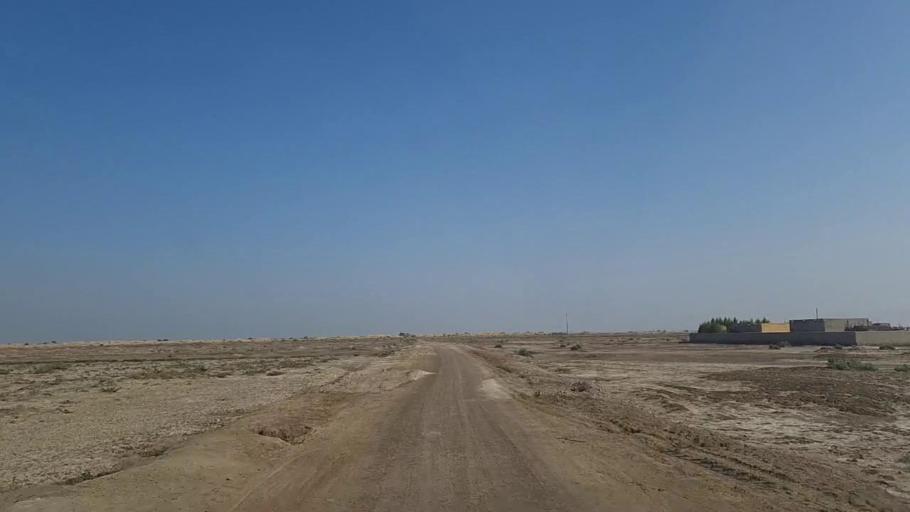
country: PK
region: Sindh
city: Digri
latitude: 25.0716
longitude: 69.2247
